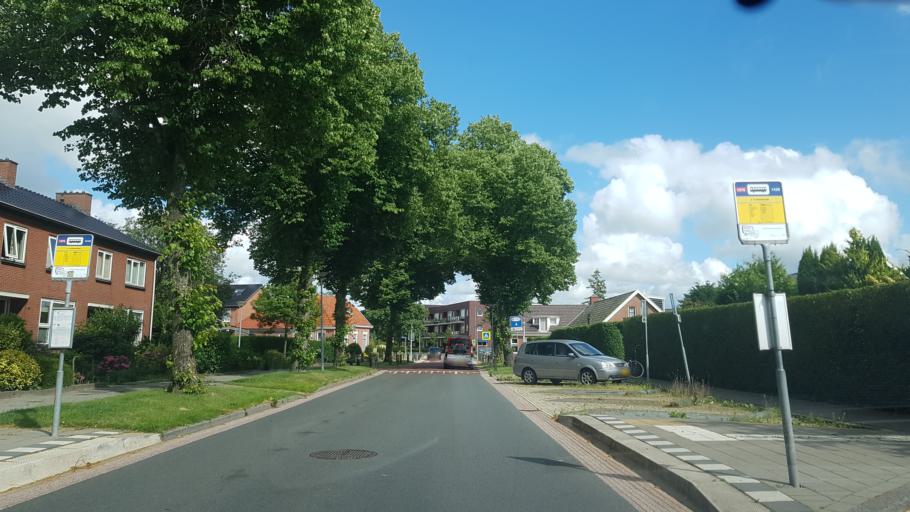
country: NL
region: Groningen
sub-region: Gemeente Bedum
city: Bedum
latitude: 53.4046
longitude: 6.6723
